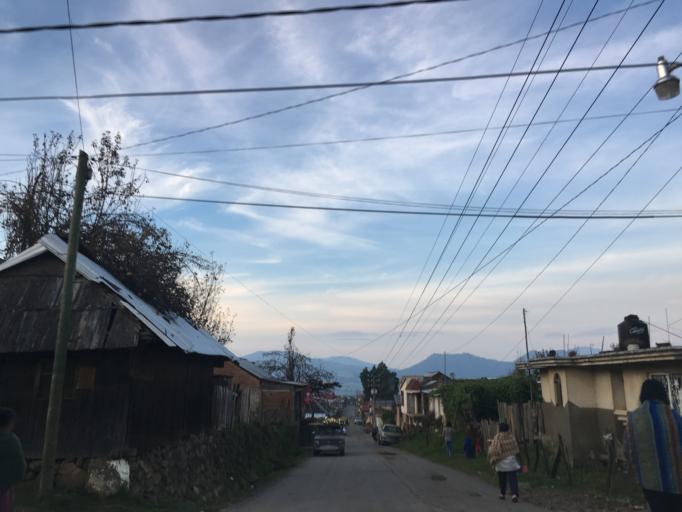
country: MX
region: Michoacan
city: Charapan
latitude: 19.6073
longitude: -102.2335
